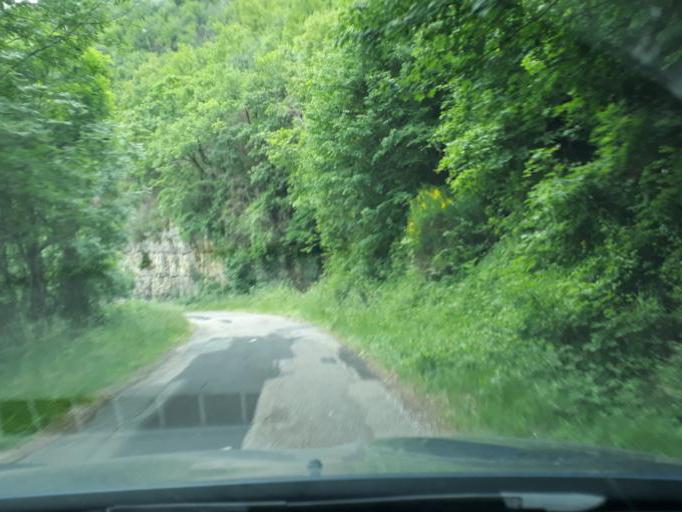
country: FR
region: Languedoc-Roussillon
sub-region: Departement de l'Herault
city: Lodeve
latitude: 43.7991
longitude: 3.2659
